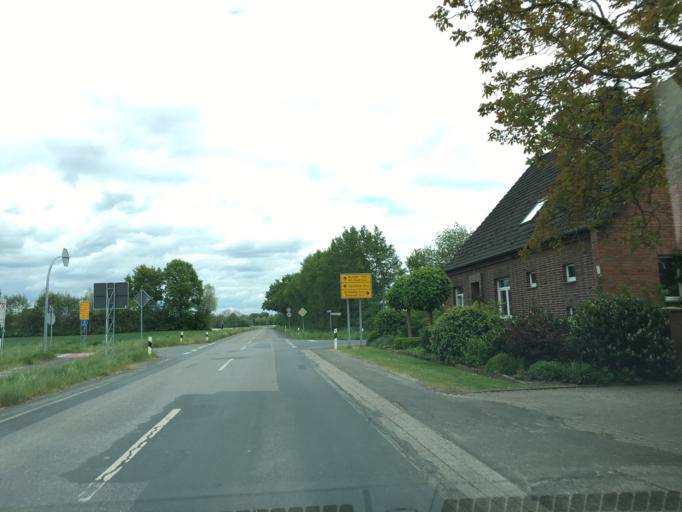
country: DE
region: North Rhine-Westphalia
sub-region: Regierungsbezirk Munster
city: Havixbeck
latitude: 51.9529
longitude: 7.5090
